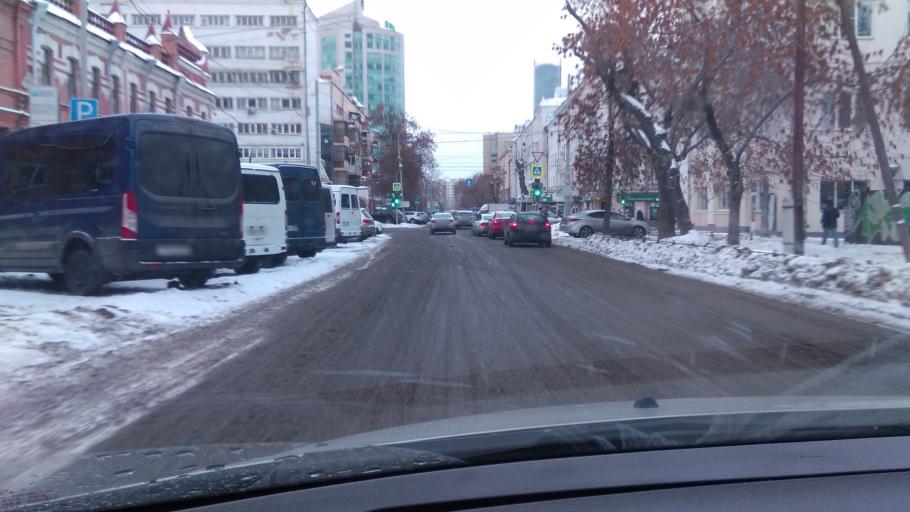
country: RU
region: Sverdlovsk
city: Yekaterinburg
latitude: 56.8326
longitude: 60.5927
